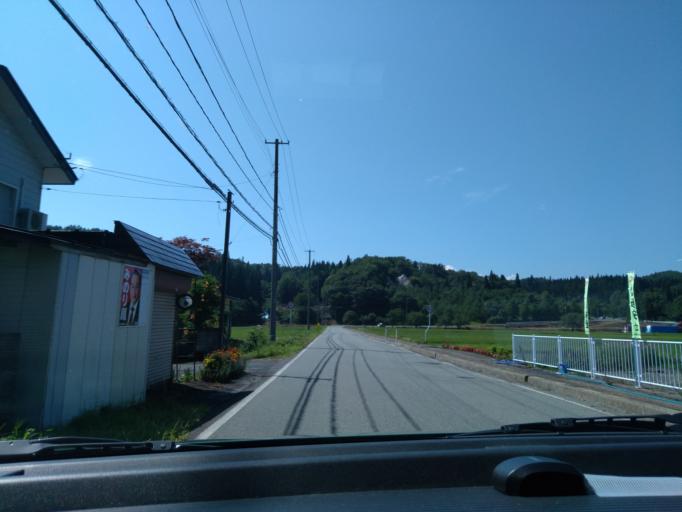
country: JP
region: Akita
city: Kakunodatemachi
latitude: 39.7327
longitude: 140.7082
